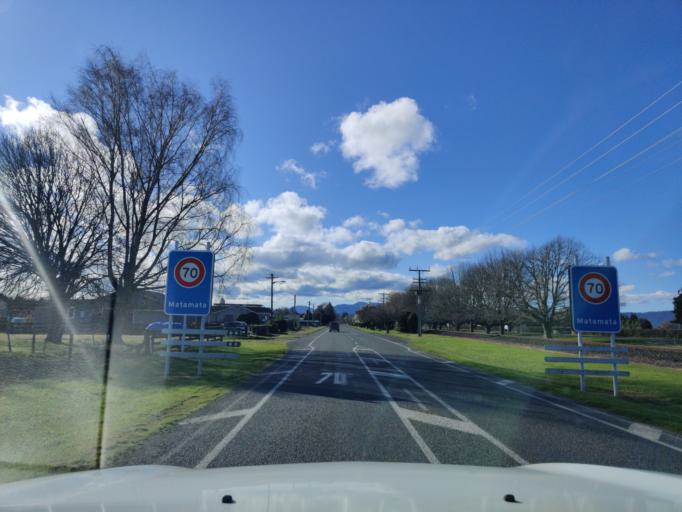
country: NZ
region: Waikato
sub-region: Matamata-Piako District
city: Matamata
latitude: -37.8297
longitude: 175.7681
